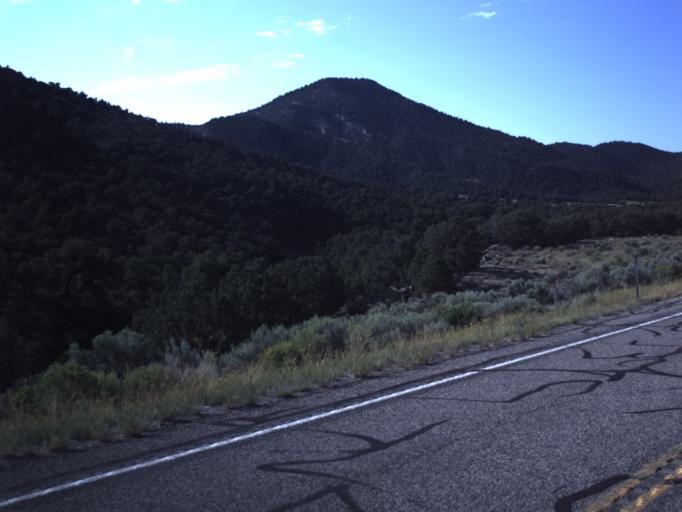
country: US
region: Utah
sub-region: Wayne County
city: Loa
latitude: 38.7435
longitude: -111.3944
